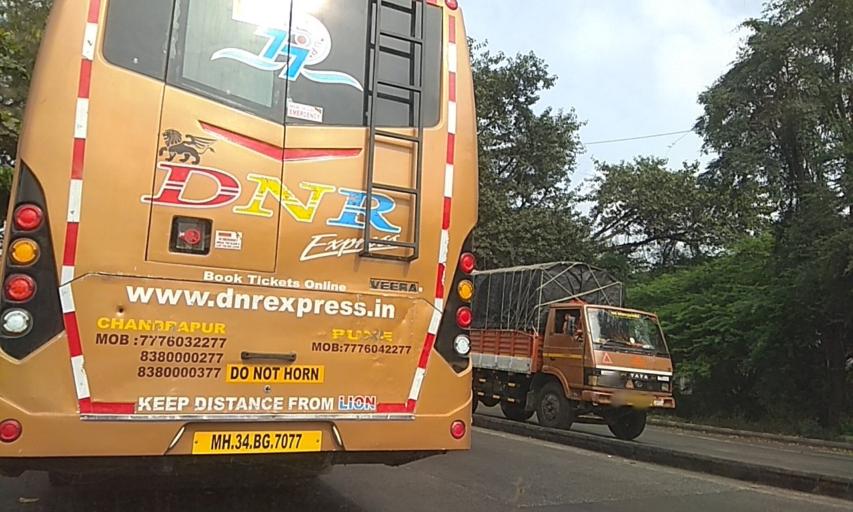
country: IN
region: Maharashtra
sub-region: Pune Division
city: Khadki
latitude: 18.5544
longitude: 73.8481
